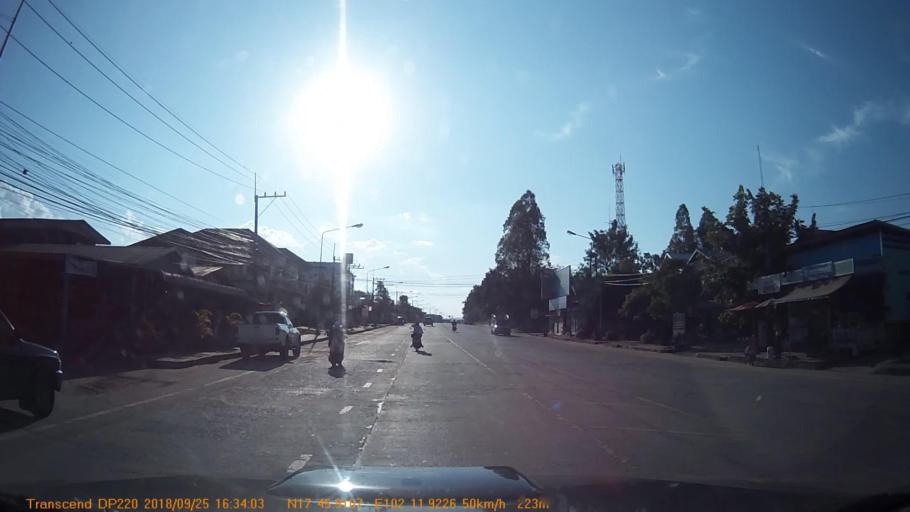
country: TH
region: Changwat Udon Thani
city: Nam Som
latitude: 17.7652
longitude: 102.1986
